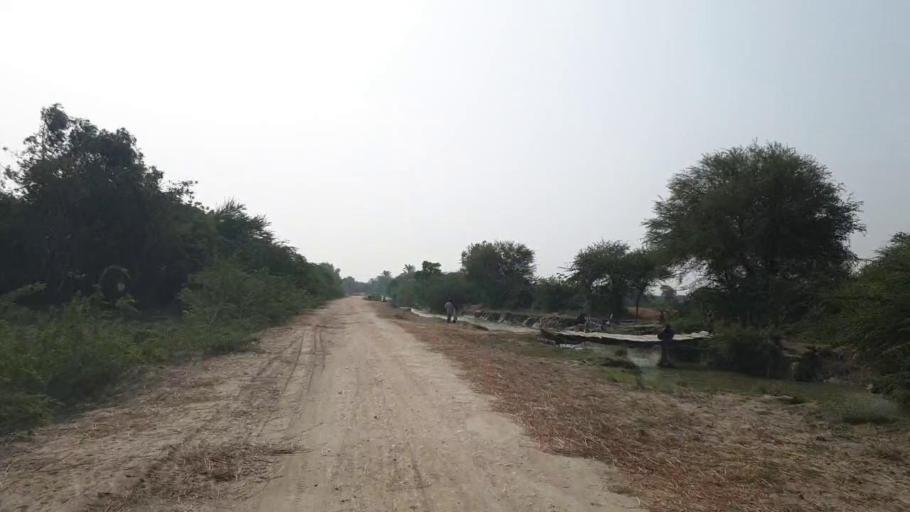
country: PK
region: Sindh
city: Kario
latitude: 24.7578
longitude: 68.5637
